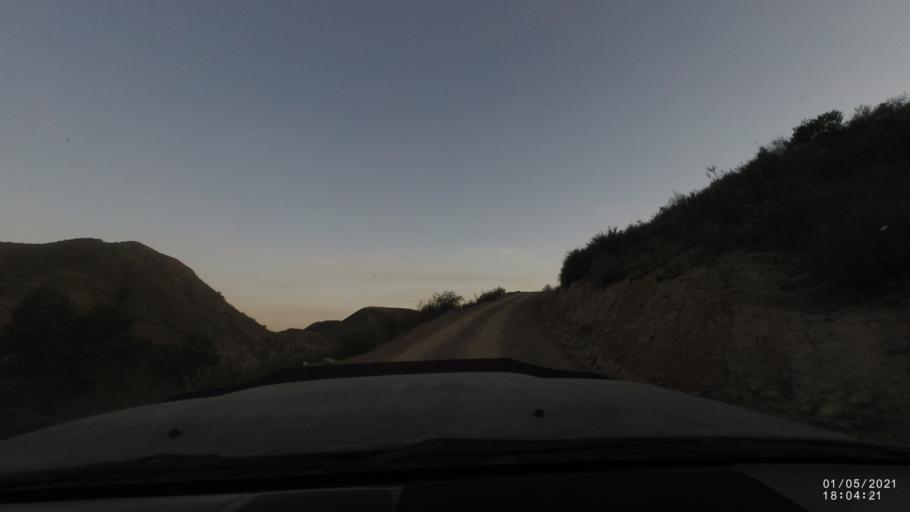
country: BO
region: Cochabamba
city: Capinota
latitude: -17.6891
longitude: -66.1792
